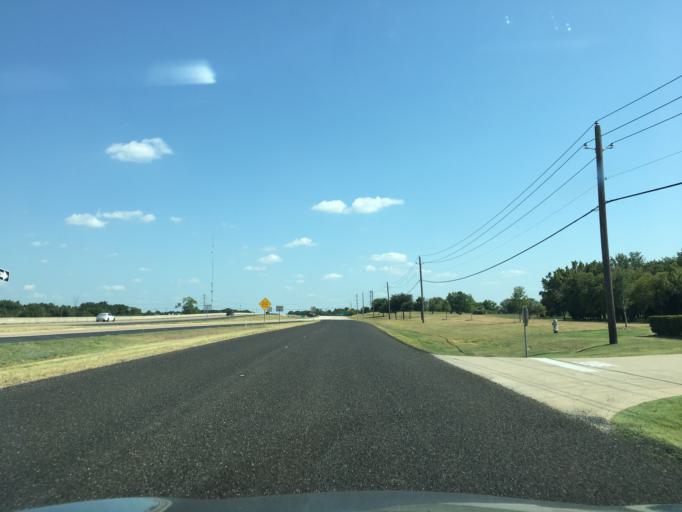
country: US
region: Texas
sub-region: Tarrant County
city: Kennedale
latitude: 32.6368
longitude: -97.1794
